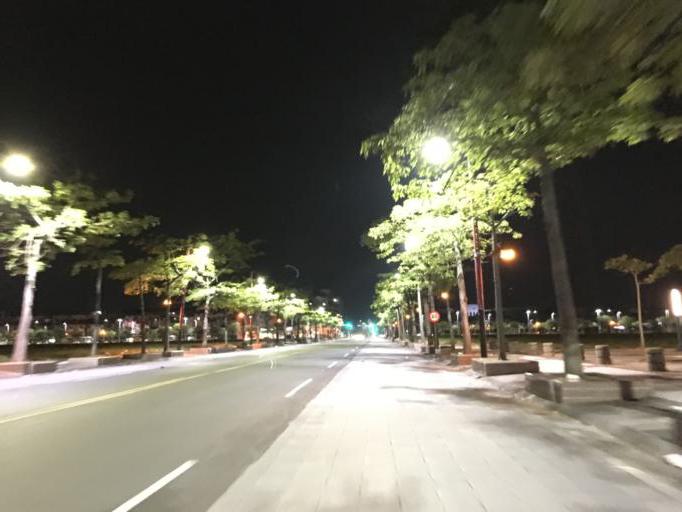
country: TW
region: Taiwan
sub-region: Chiayi
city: Taibao
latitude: 23.4623
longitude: 120.2962
